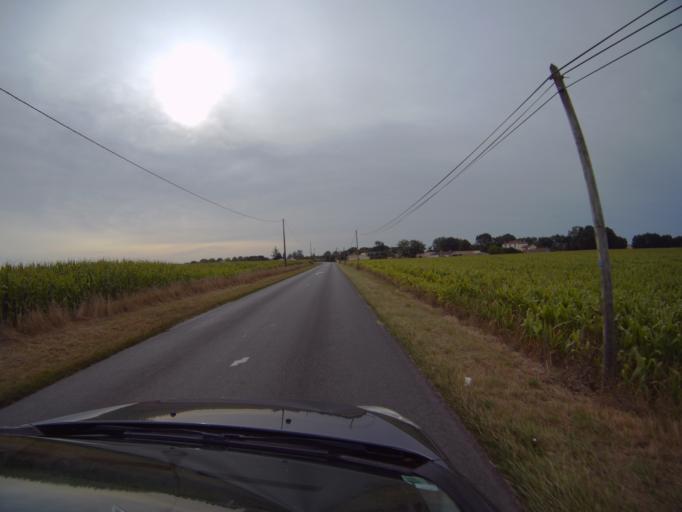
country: FR
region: Pays de la Loire
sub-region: Departement de la Vendee
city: Angles
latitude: 46.4100
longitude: -1.4482
